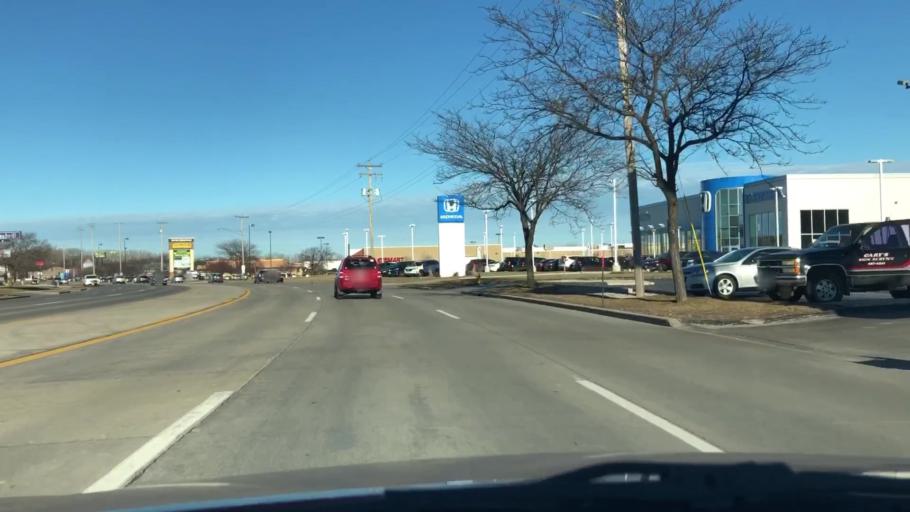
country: US
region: Wisconsin
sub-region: Brown County
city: Ashwaubenon
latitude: 44.4716
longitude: -88.0754
